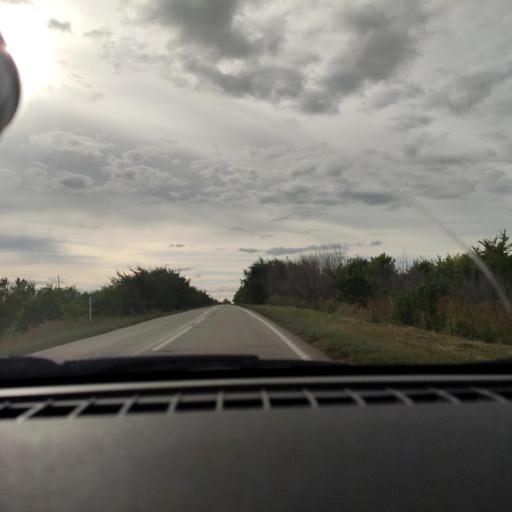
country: RU
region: Samara
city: Georgiyevka
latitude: 53.4224
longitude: 50.8376
